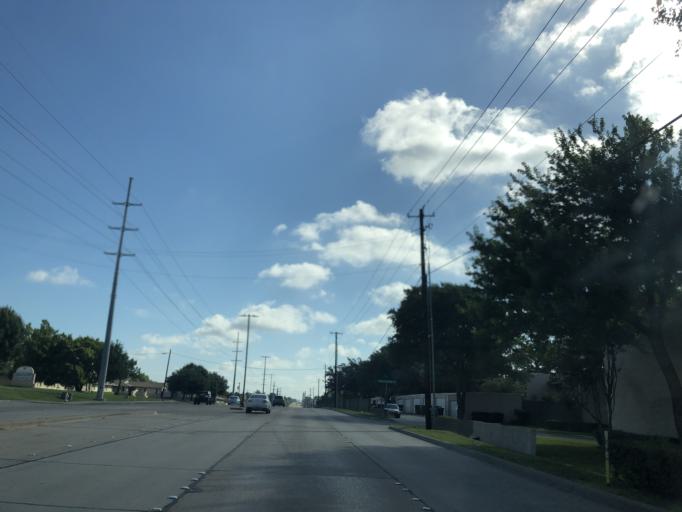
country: US
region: Texas
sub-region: Dallas County
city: Garland
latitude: 32.8652
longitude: -96.6378
